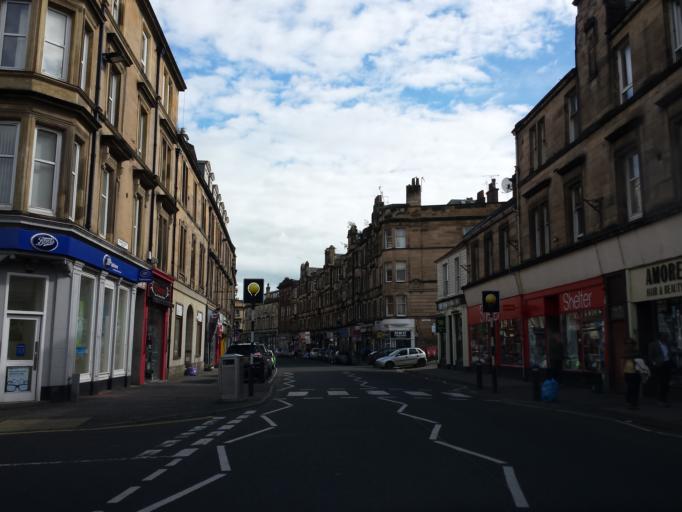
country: GB
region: Scotland
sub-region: Stirling
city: Stirling
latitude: 56.1210
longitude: -3.9386
